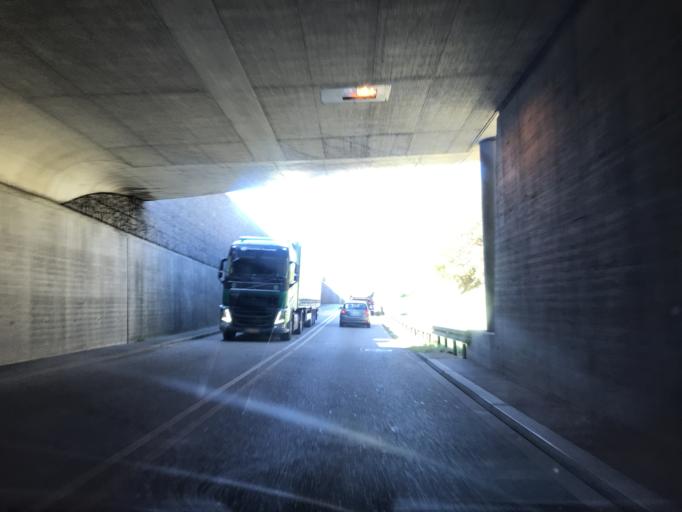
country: DE
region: Baden-Wuerttemberg
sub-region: Freiburg Region
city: Rheinfelden (Baden)
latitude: 47.5665
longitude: 7.7778
